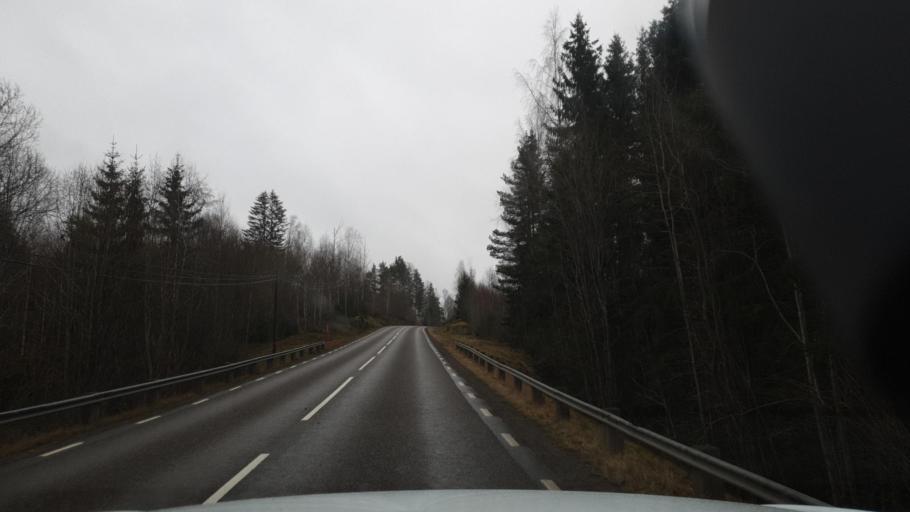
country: SE
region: Vaermland
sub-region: Eda Kommun
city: Amotfors
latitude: 59.7528
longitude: 12.3655
